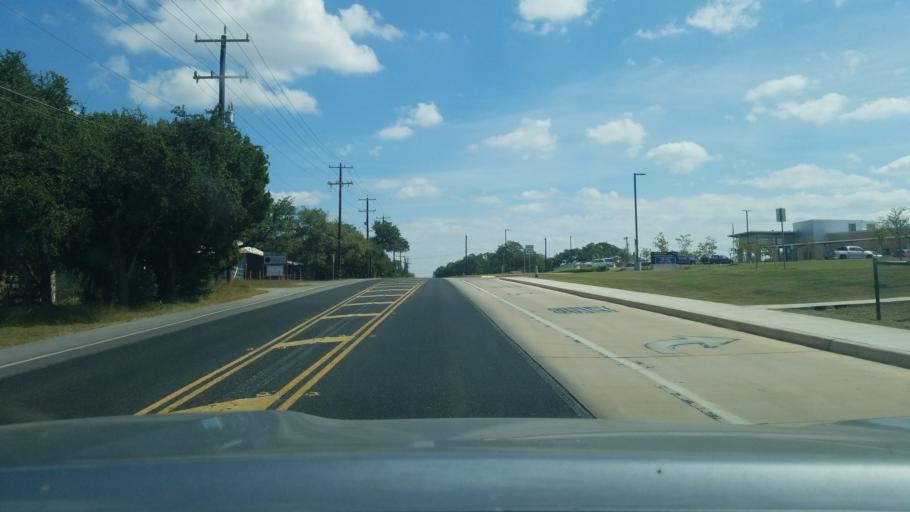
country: US
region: Texas
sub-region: Bexar County
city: Fair Oaks Ranch
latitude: 29.7311
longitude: -98.6597
